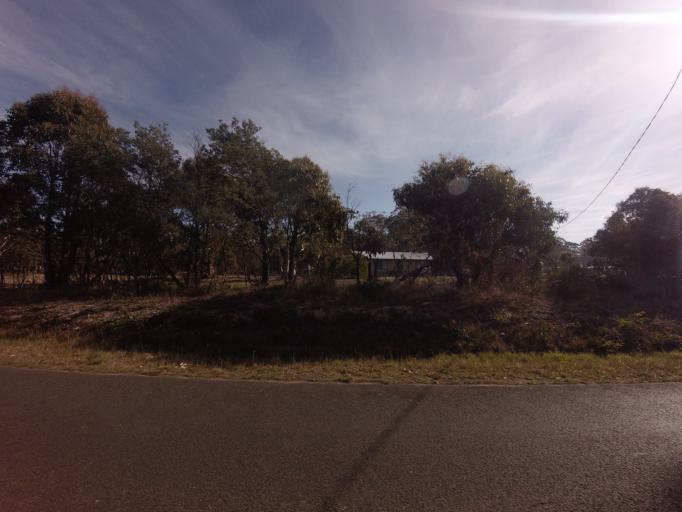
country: AU
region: Tasmania
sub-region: Sorell
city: Sorell
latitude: -42.4645
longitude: 147.4613
